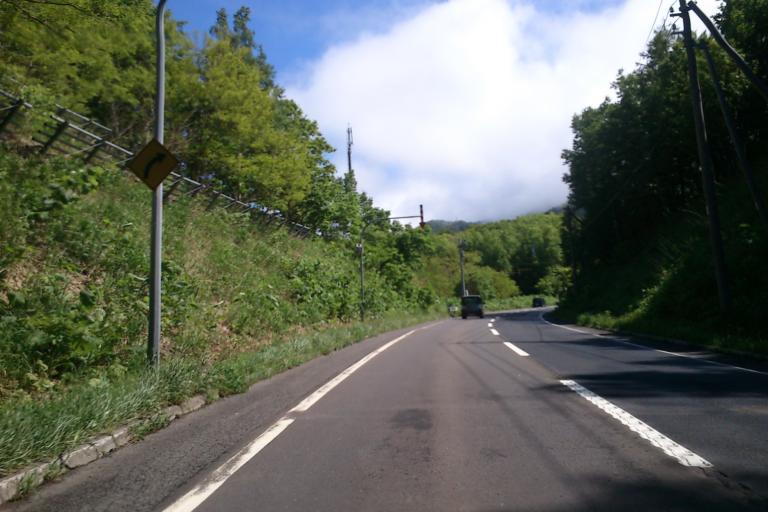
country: JP
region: Hokkaido
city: Ishikari
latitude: 43.5101
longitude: 141.3759
